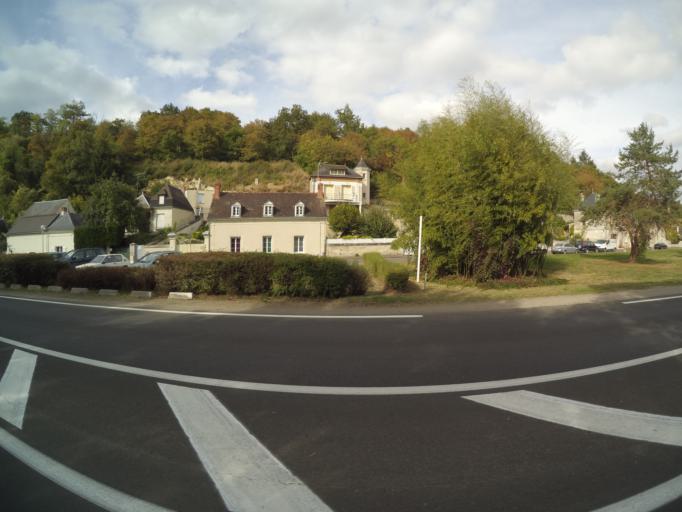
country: FR
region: Centre
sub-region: Departement d'Indre-et-Loire
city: Saint-Etienne-de-Chigny
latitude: 47.3689
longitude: 0.5138
